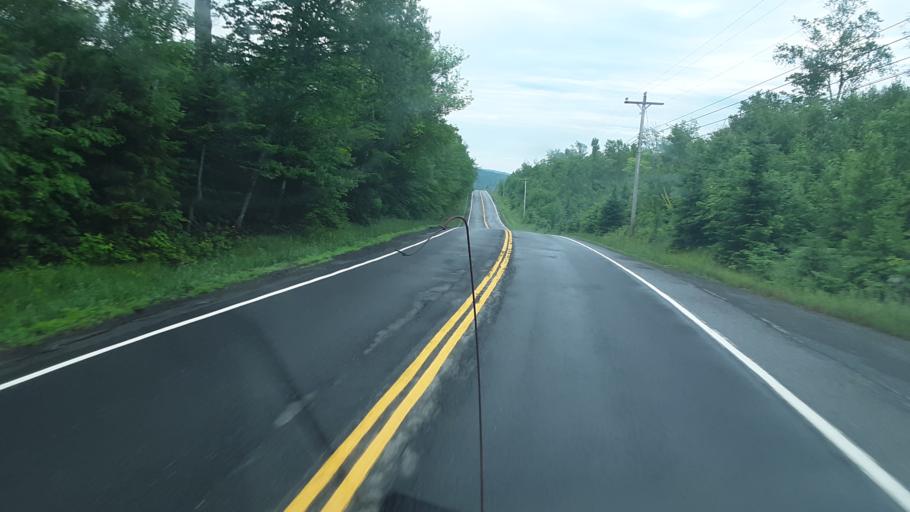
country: US
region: Maine
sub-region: Penobscot County
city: Patten
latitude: 46.1150
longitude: -68.4085
